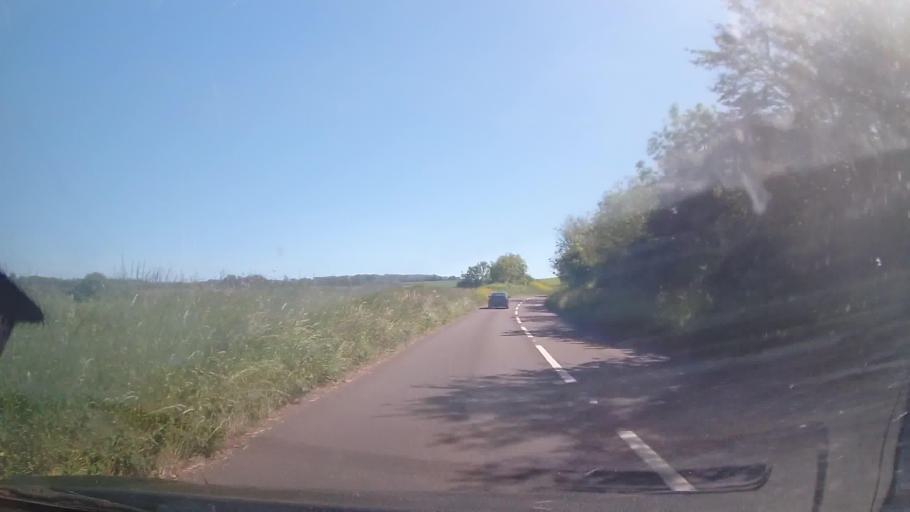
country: GB
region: England
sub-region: Borough of Torbay
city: Brixham
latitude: 50.3938
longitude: -3.5536
